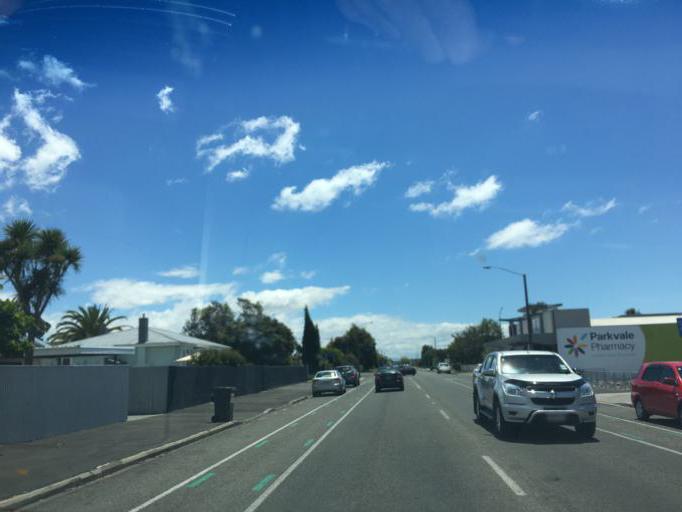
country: NZ
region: Hawke's Bay
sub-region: Hastings District
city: Hastings
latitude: -39.6469
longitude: 176.8539
